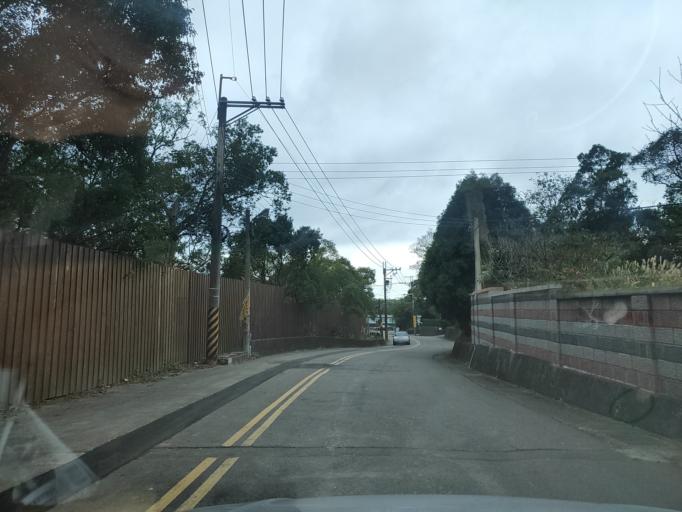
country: TW
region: Taiwan
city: Fengyuan
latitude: 24.3793
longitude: 120.7590
